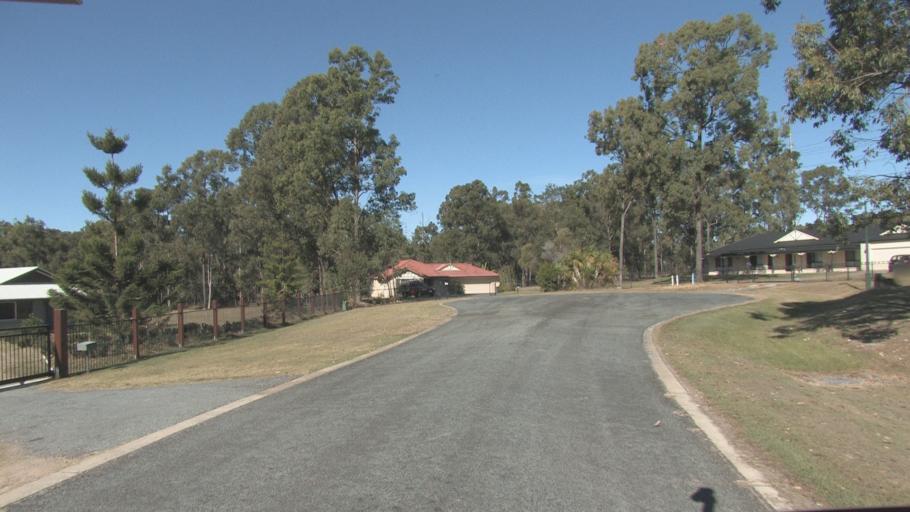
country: AU
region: Queensland
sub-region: Logan
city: North Maclean
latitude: -27.7340
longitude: 152.9654
